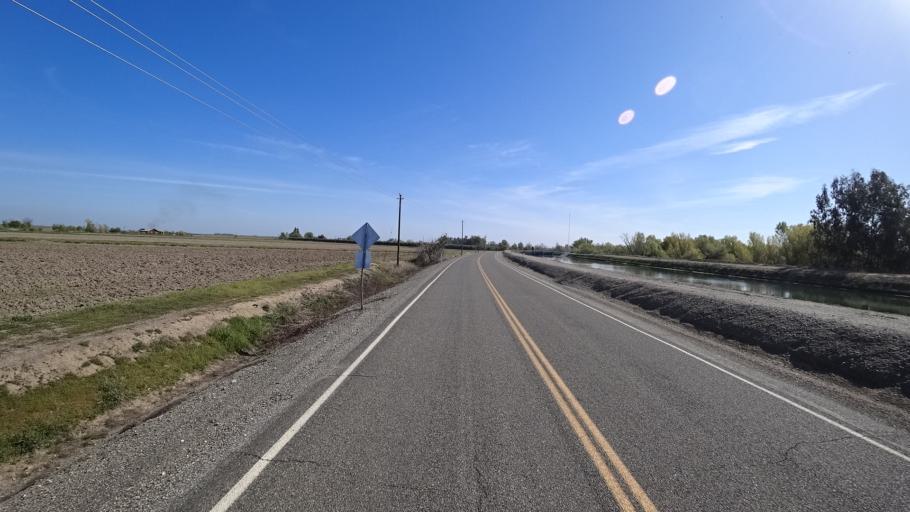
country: US
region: California
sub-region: Glenn County
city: Willows
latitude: 39.5401
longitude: -122.1722
